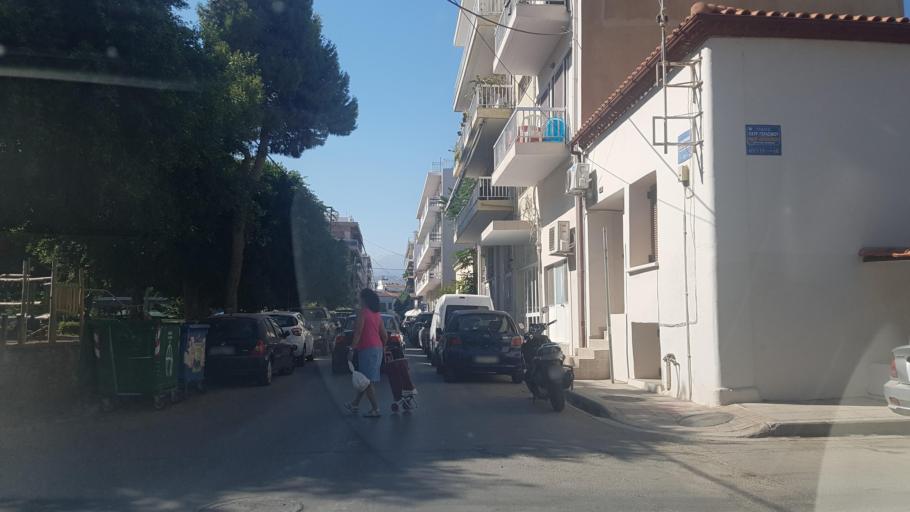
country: GR
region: Crete
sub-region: Nomos Chanias
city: Chania
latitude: 35.5151
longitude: 24.0124
